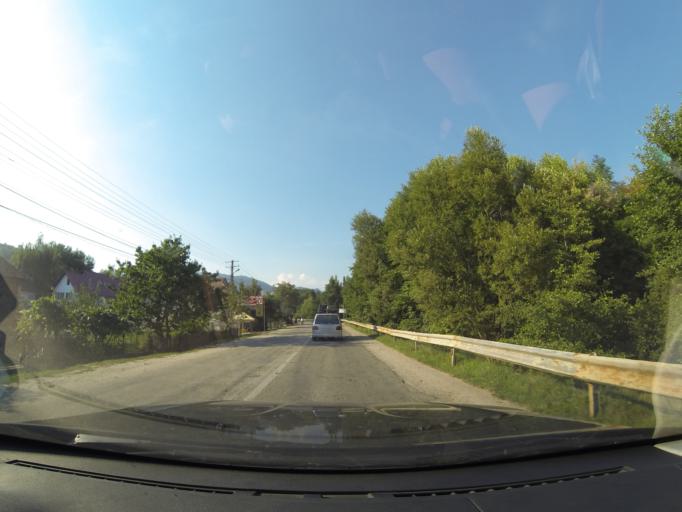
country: RO
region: Arges
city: Poenari
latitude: 45.3216
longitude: 24.6399
